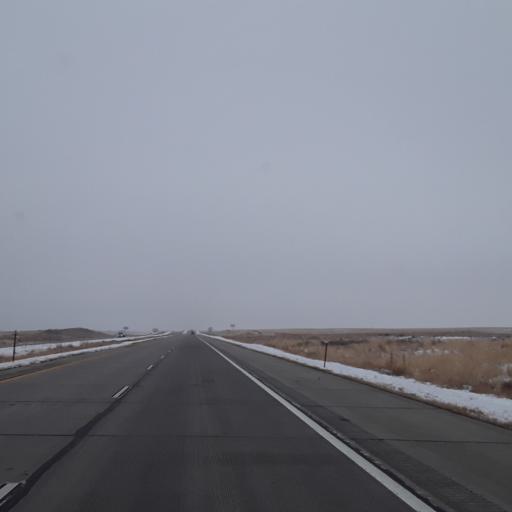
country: US
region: Colorado
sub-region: Logan County
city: Sterling
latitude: 40.5137
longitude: -103.2481
